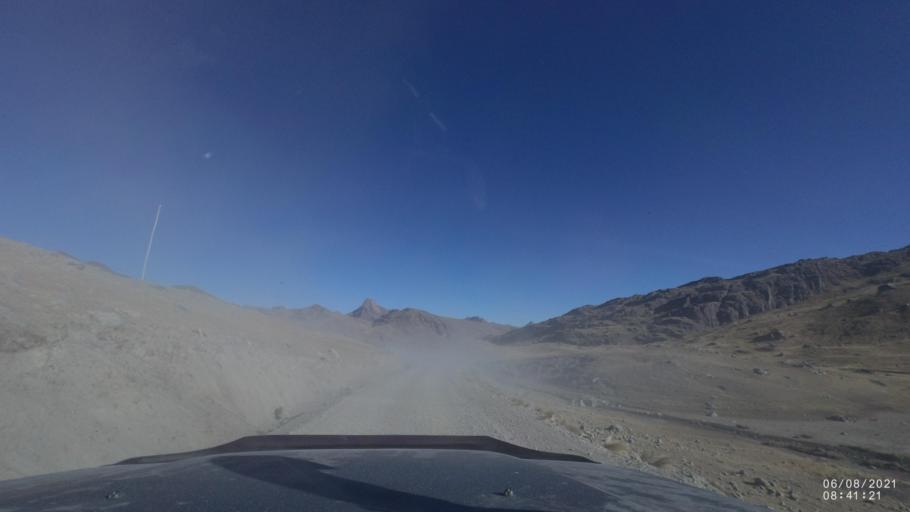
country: BO
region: Cochabamba
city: Sipe Sipe
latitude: -17.1691
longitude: -66.4066
